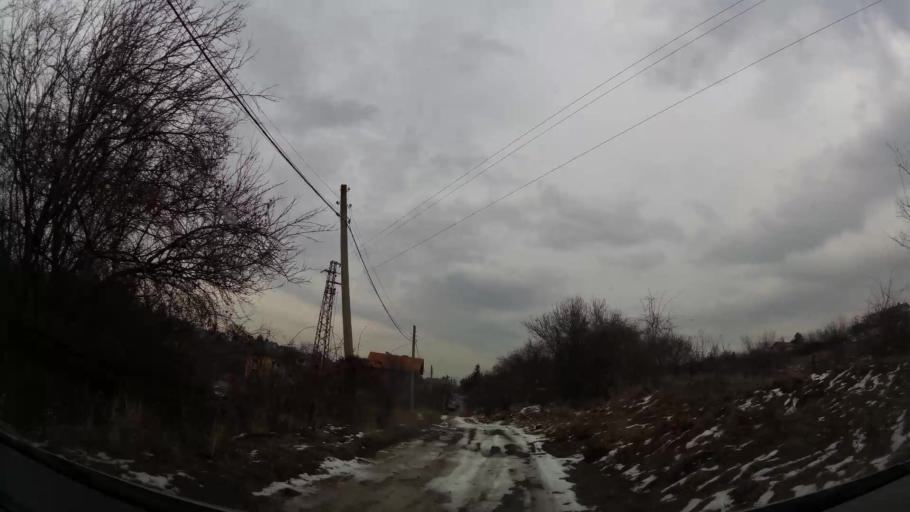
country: BG
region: Sofiya
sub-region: Obshtina Bozhurishte
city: Bozhurishte
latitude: 42.6941
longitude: 23.2180
